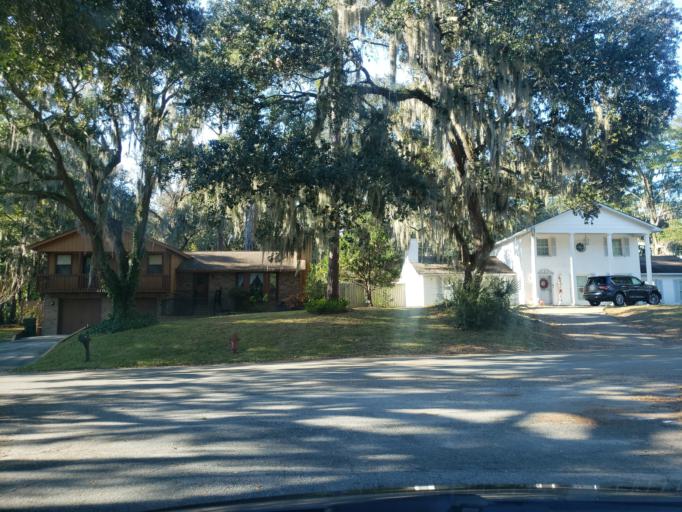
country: US
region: Georgia
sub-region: Chatham County
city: Whitemarsh Island
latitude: 32.0553
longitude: -81.0194
